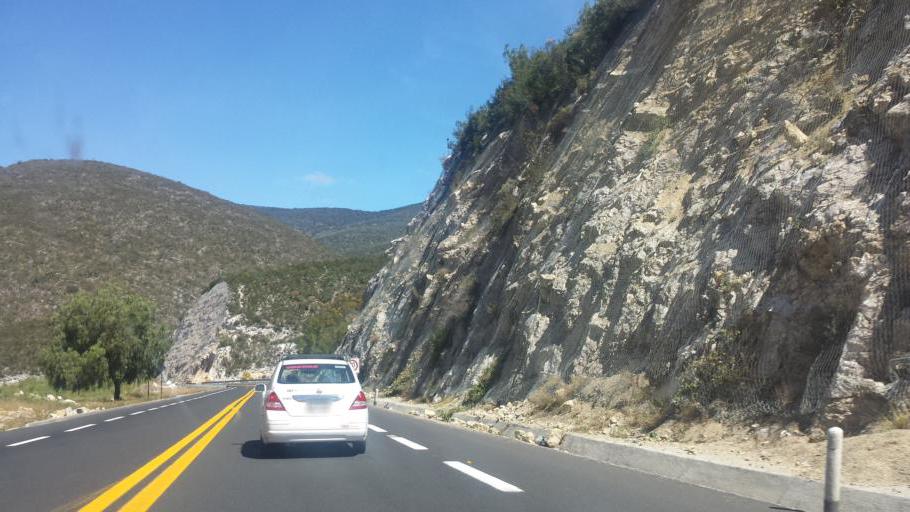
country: MX
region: Puebla
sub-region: San Jose Miahuatlan
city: San Pedro Tetitlan
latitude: 18.0210
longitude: -97.3506
